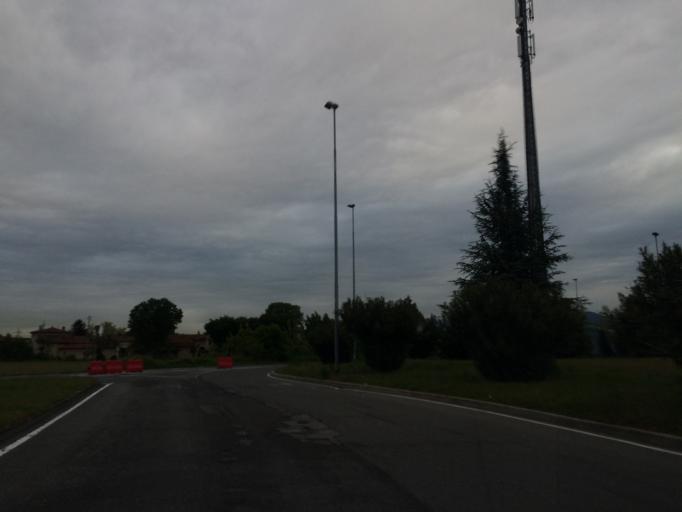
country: IT
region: Lombardy
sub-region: Provincia di Brescia
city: San Zeno Naviglio
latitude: 45.4978
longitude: 10.2192
